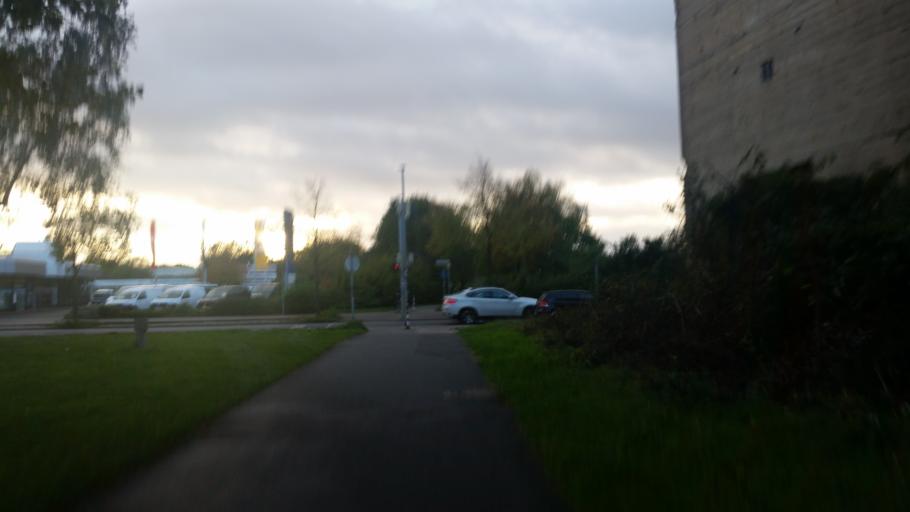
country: DE
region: Lower Saxony
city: Hannover
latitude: 52.4007
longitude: 9.7640
